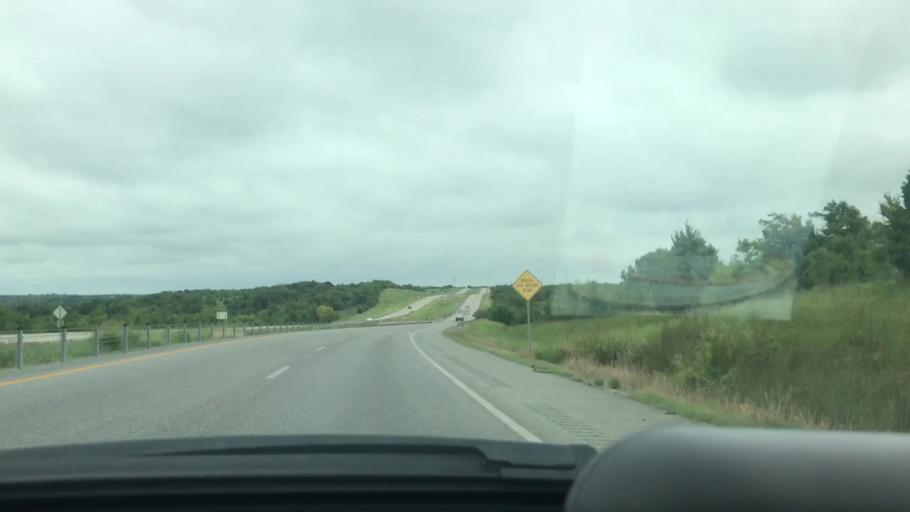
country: US
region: Oklahoma
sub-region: Pittsburg County
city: McAlester
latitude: 34.6789
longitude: -95.9323
